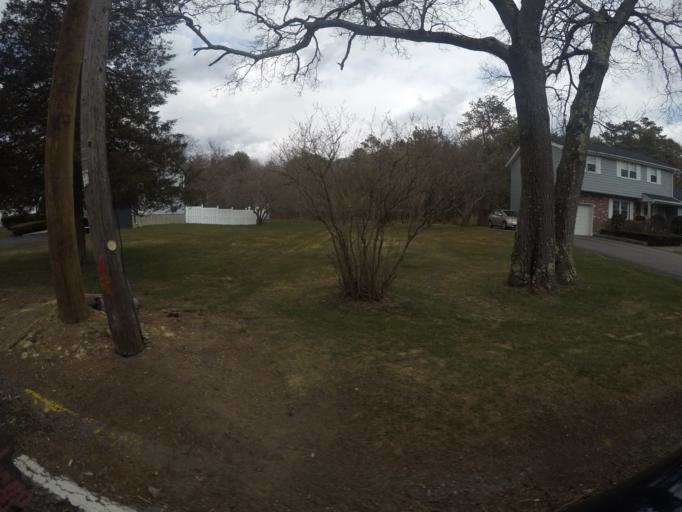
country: US
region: Massachusetts
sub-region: Bristol County
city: Easton
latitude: 42.0567
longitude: -71.1256
